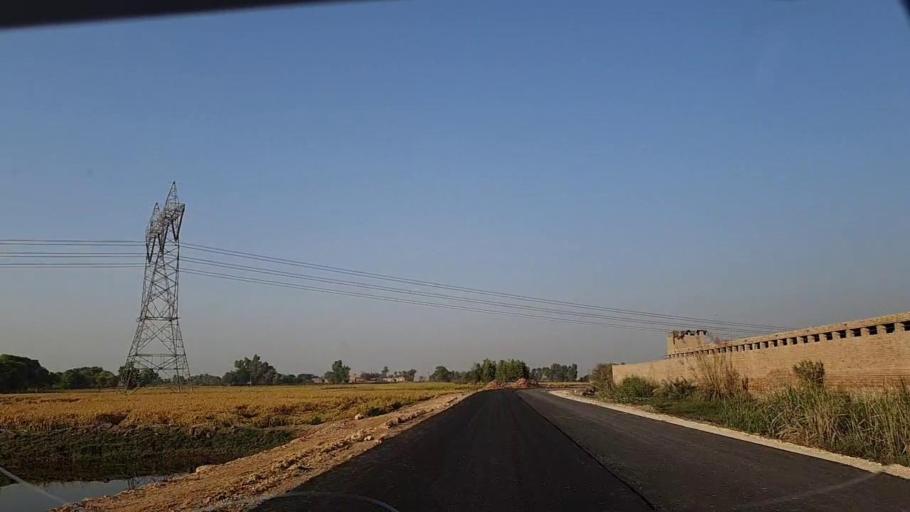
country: PK
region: Sindh
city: Rustam jo Goth
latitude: 27.9686
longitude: 68.8016
